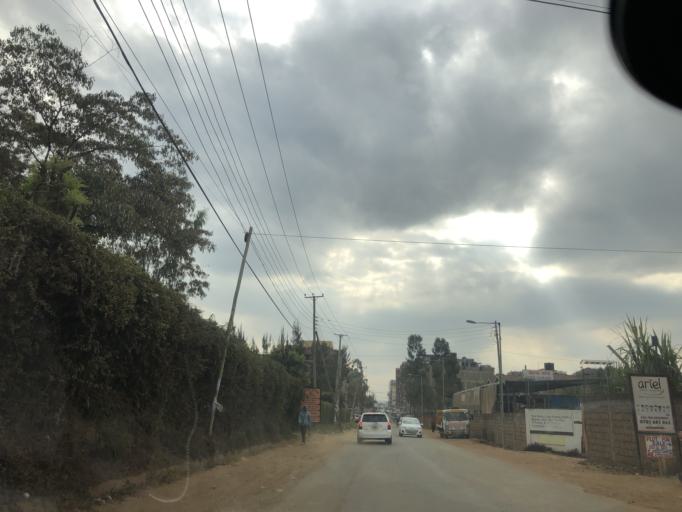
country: KE
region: Kiambu
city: Kiambu
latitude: -1.2117
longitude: 36.8888
